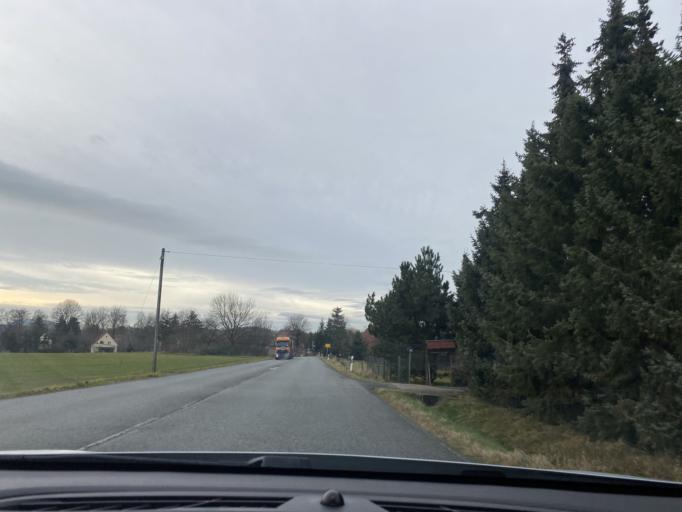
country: DE
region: Saxony
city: Sohland am Rotstein
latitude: 51.1356
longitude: 14.7761
